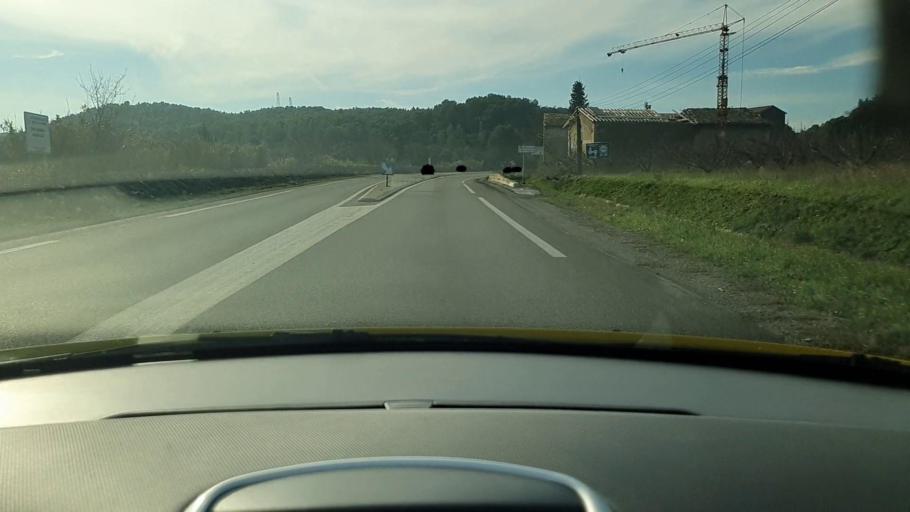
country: FR
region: Languedoc-Roussillon
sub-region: Departement du Gard
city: Vallabregues
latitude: 43.8328
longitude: 4.6196
